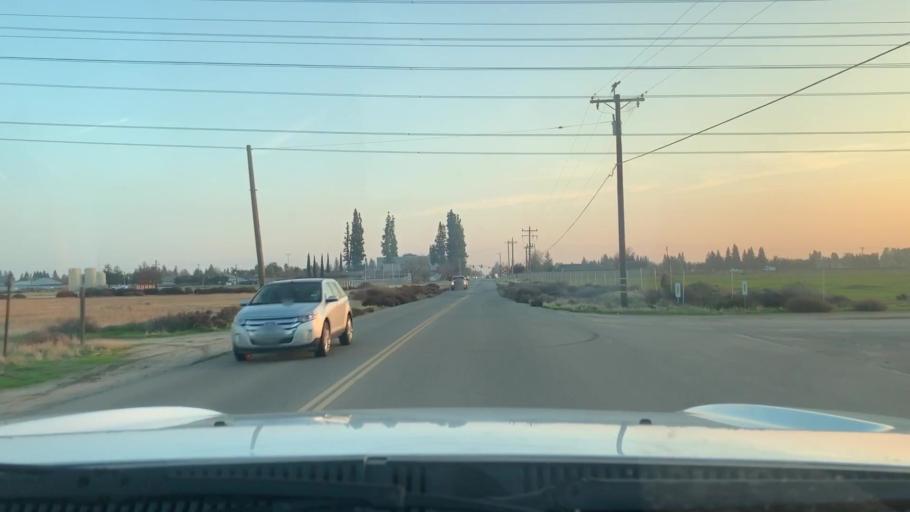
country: US
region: California
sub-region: Kern County
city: Rosedale
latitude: 35.3872
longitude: -119.1811
